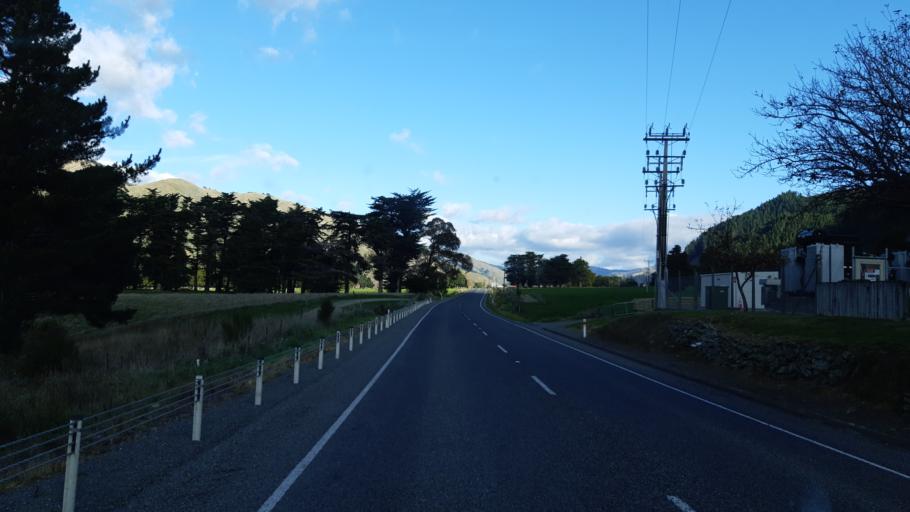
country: NZ
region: Marlborough
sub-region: Marlborough District
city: Picton
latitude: -41.2960
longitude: 173.7701
